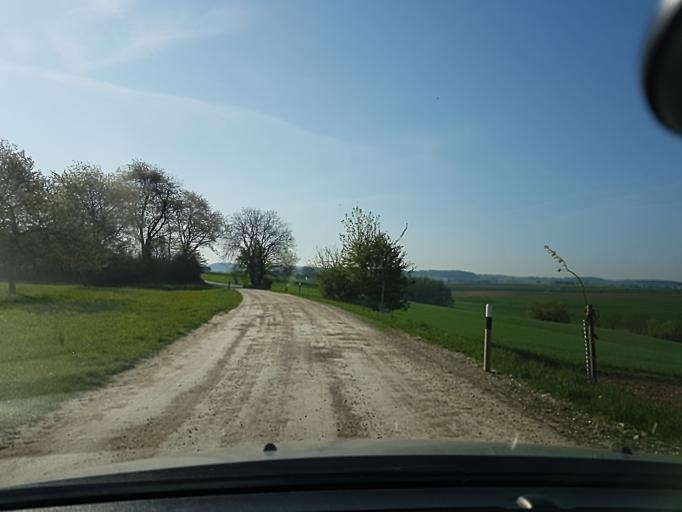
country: DE
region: Bavaria
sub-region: Lower Bavaria
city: Vilsheim
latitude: 48.4693
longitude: 12.1208
